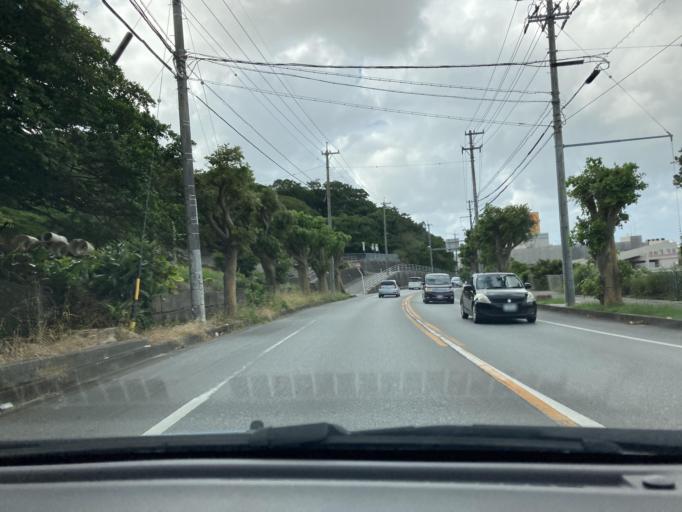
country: JP
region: Okinawa
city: Tomigusuku
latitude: 26.1729
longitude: 127.6900
